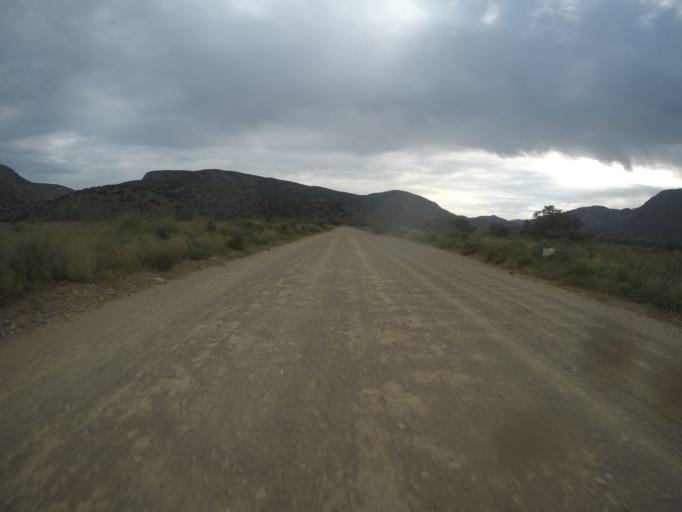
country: ZA
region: Eastern Cape
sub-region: Cacadu District Municipality
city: Willowmore
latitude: -33.5268
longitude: 23.8640
